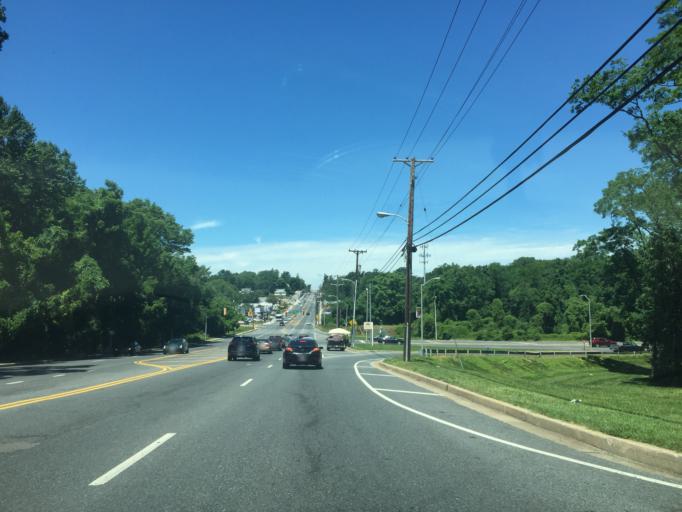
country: US
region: Maryland
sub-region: Baltimore County
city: Lochearn
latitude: 39.3356
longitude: -76.7086
